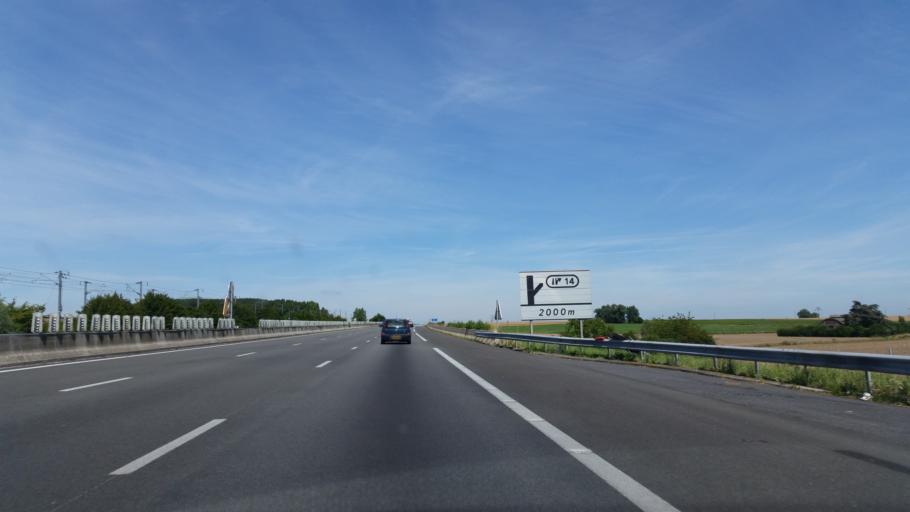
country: FR
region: Nord-Pas-de-Calais
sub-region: Departement du Pas-de-Calais
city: Bapaume
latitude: 50.0831
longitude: 2.8703
